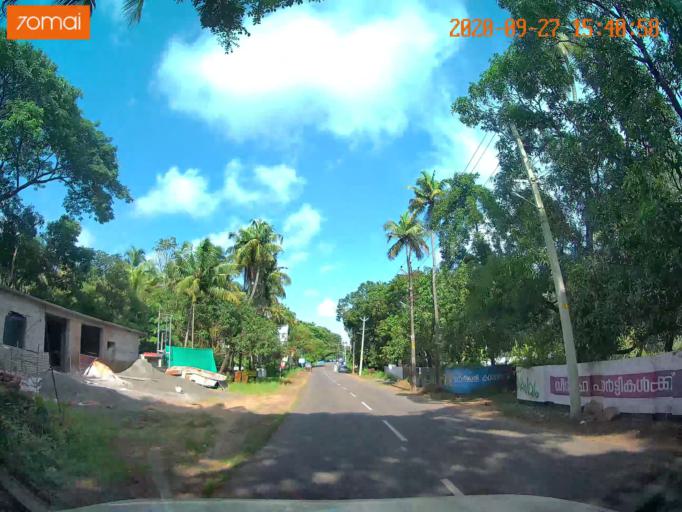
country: IN
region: Kerala
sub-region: Thrissur District
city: Thanniyam
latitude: 10.4706
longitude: 76.0910
